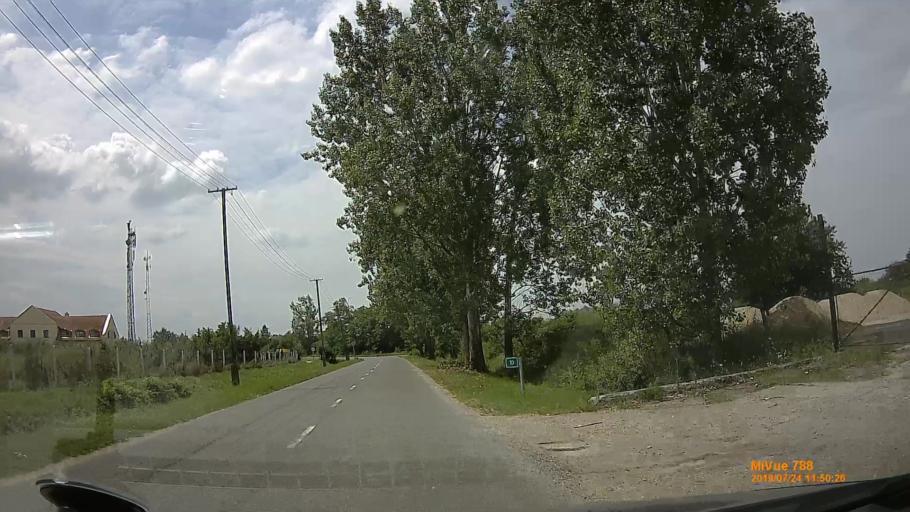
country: UA
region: Zakarpattia
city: Batiovo
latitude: 48.2406
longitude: 22.4376
